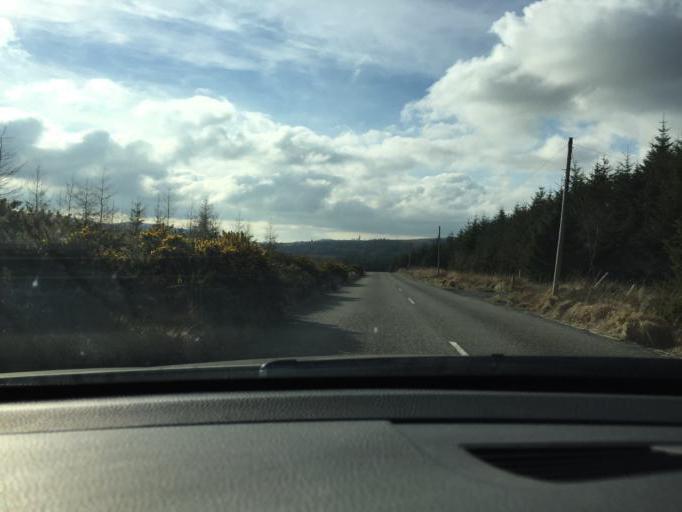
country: IE
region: Leinster
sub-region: Wicklow
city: Valleymount
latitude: 53.0593
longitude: -6.4481
